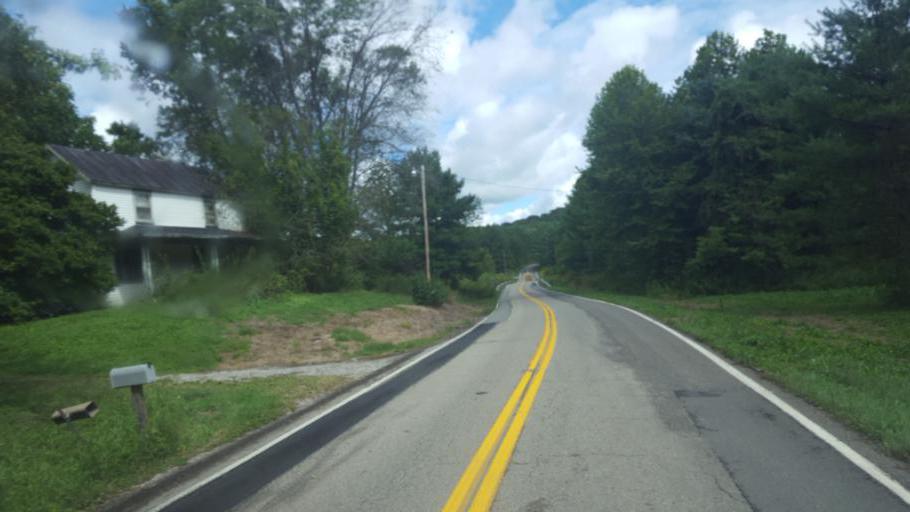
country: US
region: Ohio
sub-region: Jackson County
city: Oak Hill
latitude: 38.8857
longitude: -82.6905
